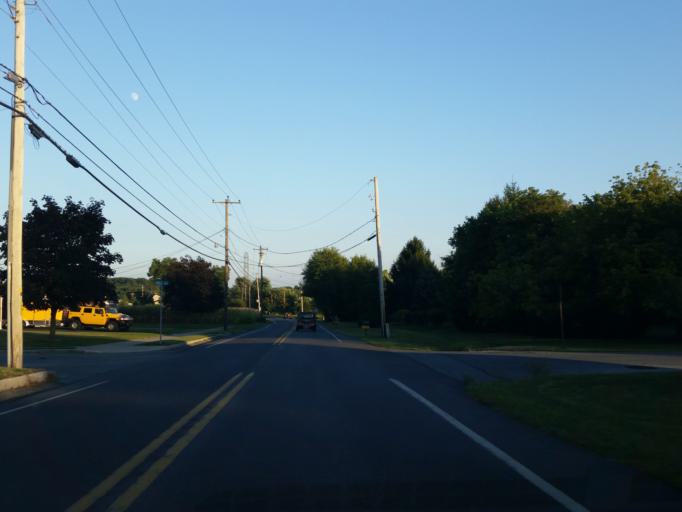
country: US
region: Pennsylvania
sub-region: Lebanon County
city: Sand Hill
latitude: 40.3779
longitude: -76.4426
